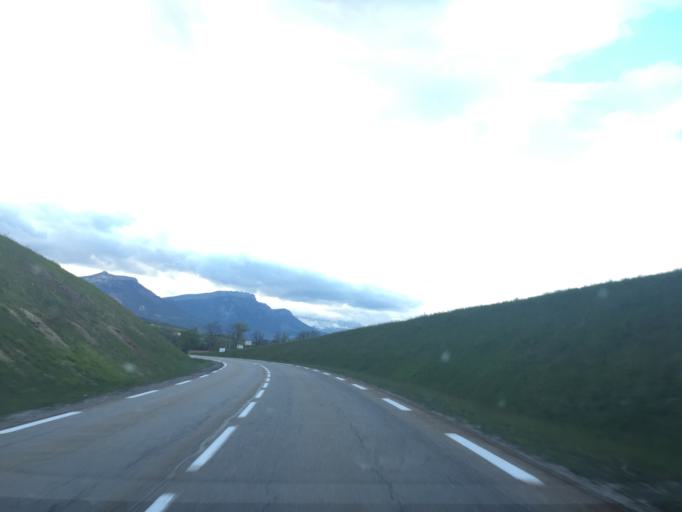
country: FR
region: Rhone-Alpes
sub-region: Departement de l'Isere
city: Mens
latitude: 44.7849
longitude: 5.6470
